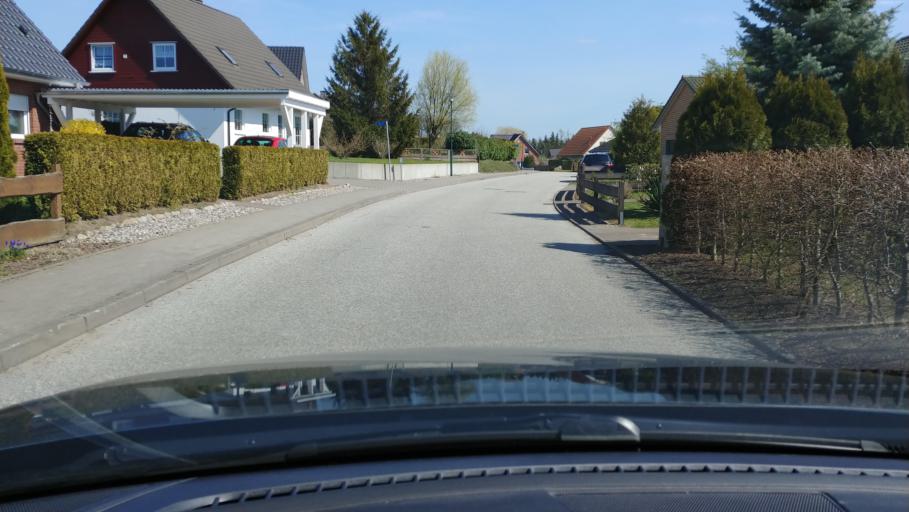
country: DE
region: Mecklenburg-Vorpommern
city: Mecklenburg
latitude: 53.8411
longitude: 11.4631
